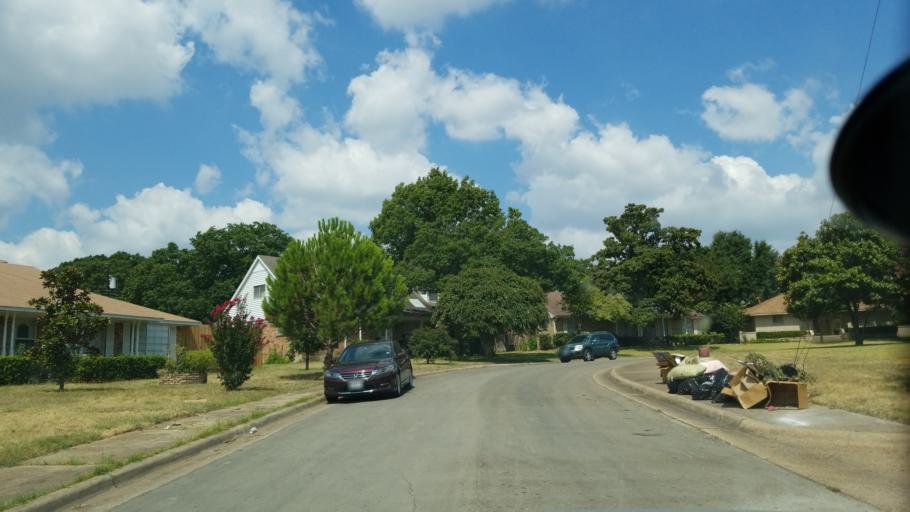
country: US
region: Texas
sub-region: Dallas County
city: Cockrell Hill
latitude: 32.6929
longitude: -96.8820
